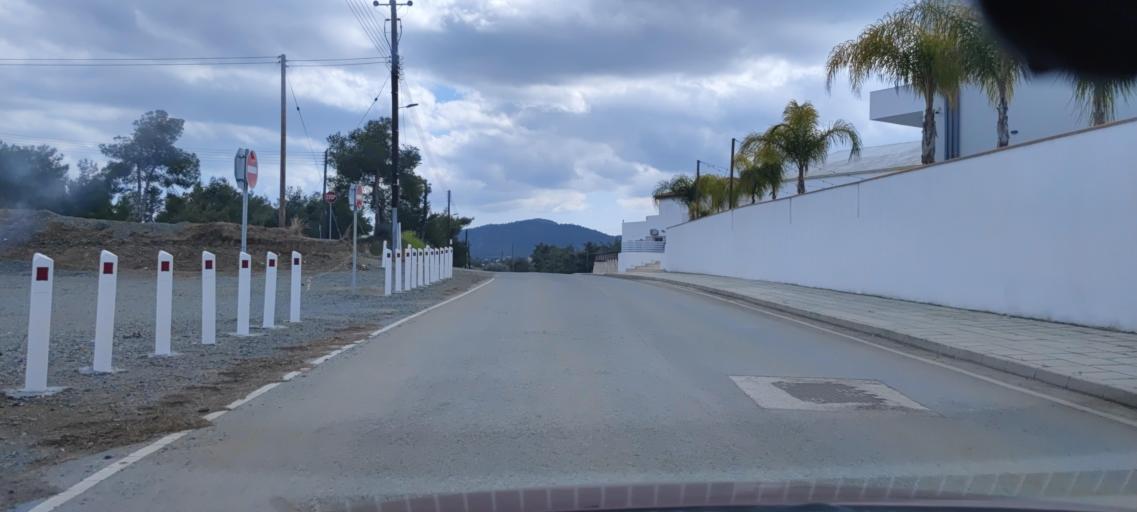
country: CY
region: Lefkosia
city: Lythrodontas
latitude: 34.9625
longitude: 33.2934
